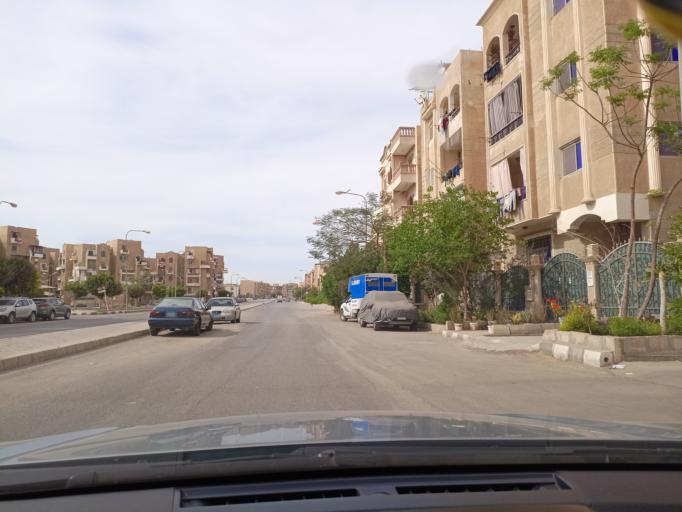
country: EG
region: Muhafazat al Qalyubiyah
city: Al Khankah
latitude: 30.2568
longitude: 31.4774
